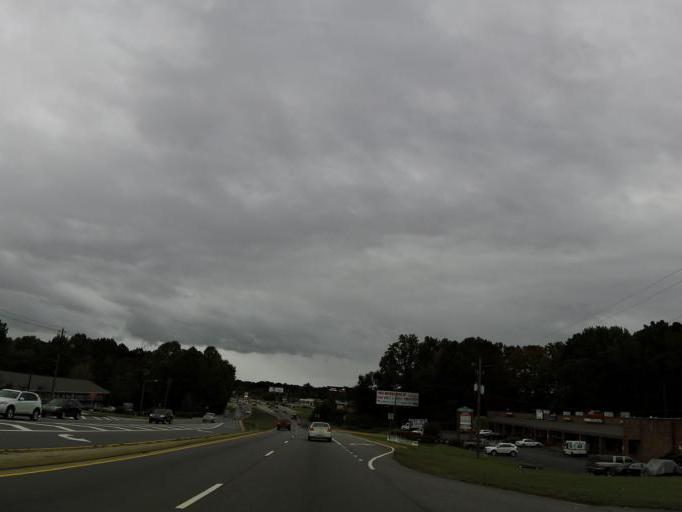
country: US
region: Georgia
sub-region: Cobb County
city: Kennesaw
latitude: 34.0183
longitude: -84.6184
